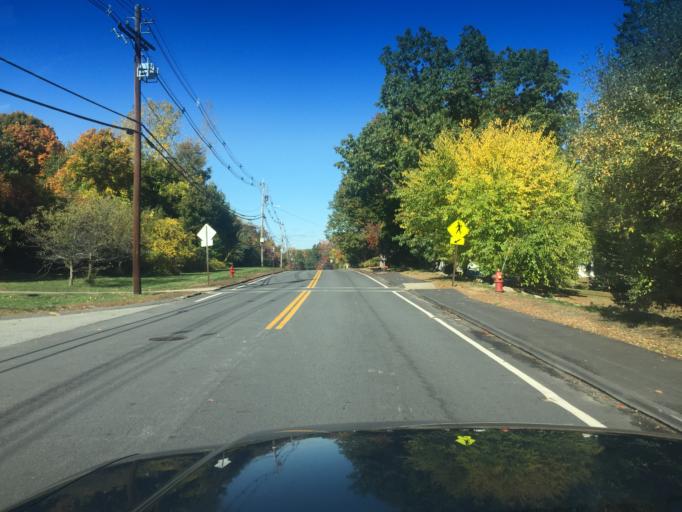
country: US
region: Massachusetts
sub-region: Middlesex County
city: Hudson
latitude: 42.3810
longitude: -71.5490
